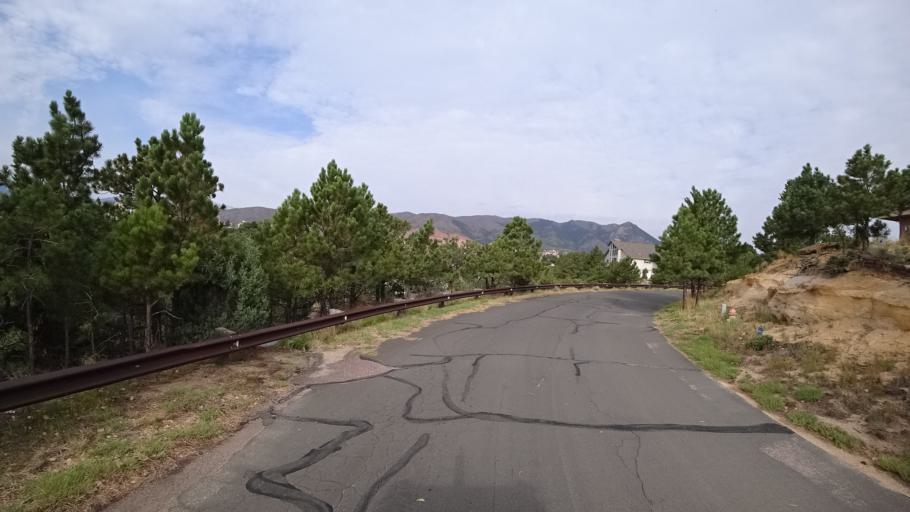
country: US
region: Colorado
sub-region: El Paso County
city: Air Force Academy
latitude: 38.9330
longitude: -104.8565
